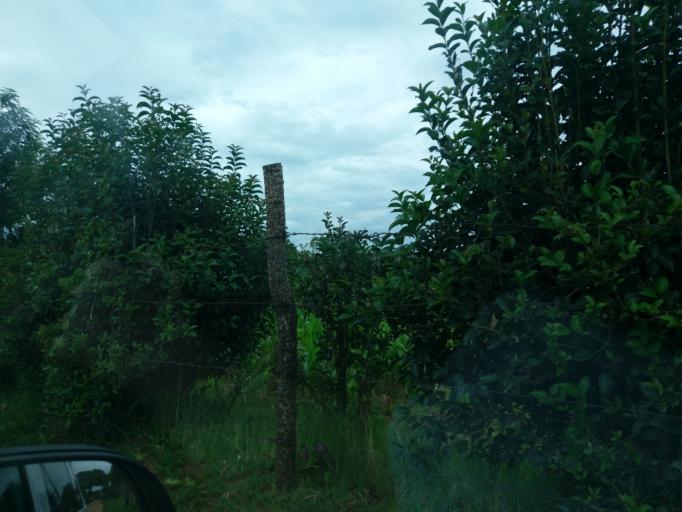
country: LS
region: Berea
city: Teyateyaneng
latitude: -29.1177
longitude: 27.9610
